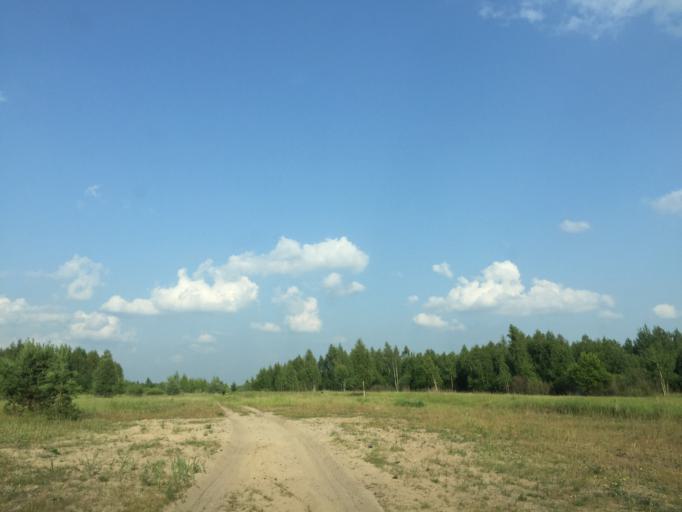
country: LV
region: Jelgava
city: Jelgava
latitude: 56.6726
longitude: 23.6620
